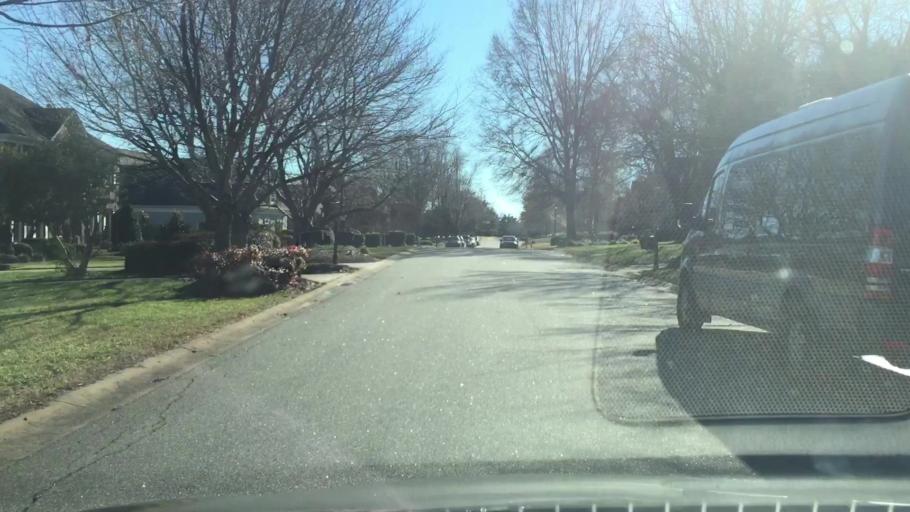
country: US
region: North Carolina
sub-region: Mecklenburg County
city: Cornelius
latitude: 35.5212
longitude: -80.8818
